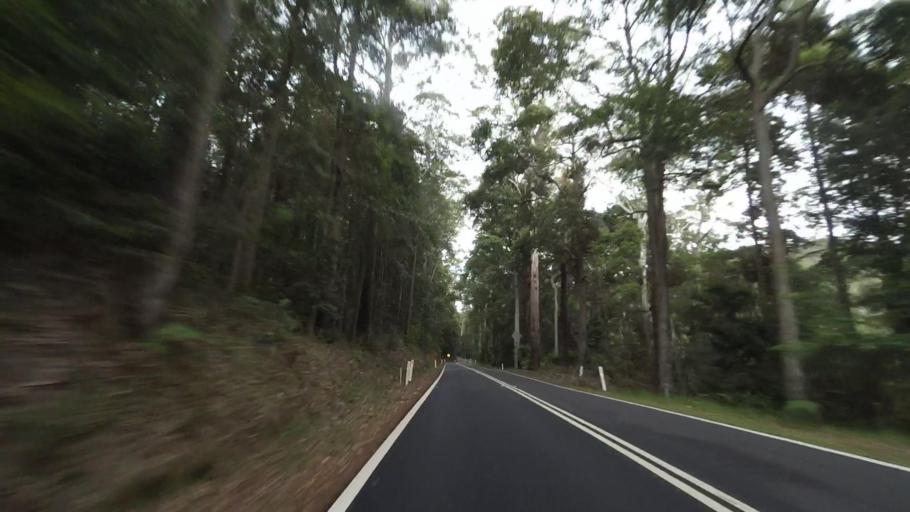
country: AU
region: New South Wales
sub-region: Wollongong
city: Helensburgh
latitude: -34.1573
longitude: 151.0187
